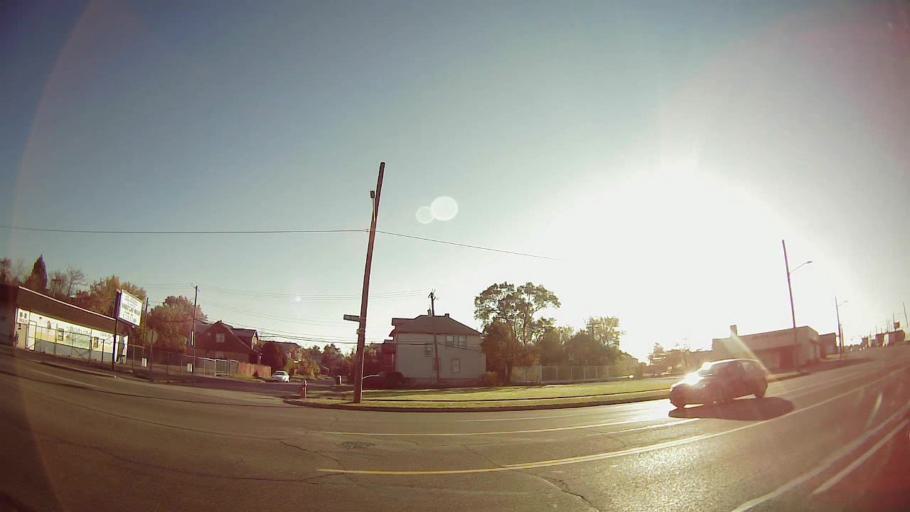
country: US
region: Michigan
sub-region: Wayne County
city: Hamtramck
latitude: 42.3901
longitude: -83.0226
